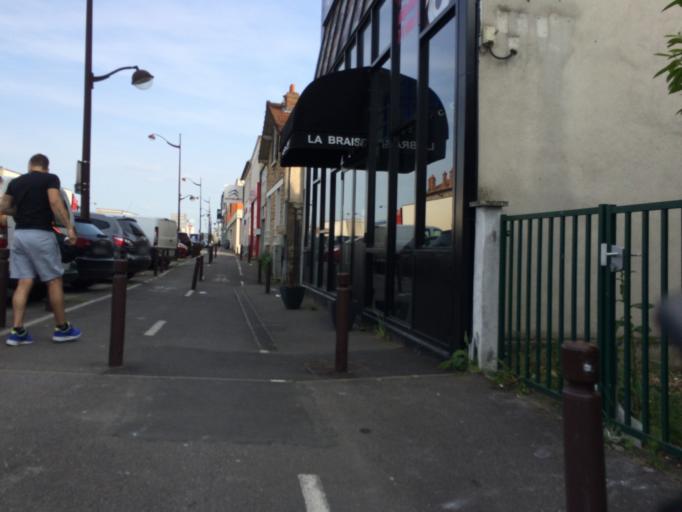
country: FR
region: Ile-de-France
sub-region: Departement de l'Essonne
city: Juvisy-sur-Orge
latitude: 48.6833
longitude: 2.3765
